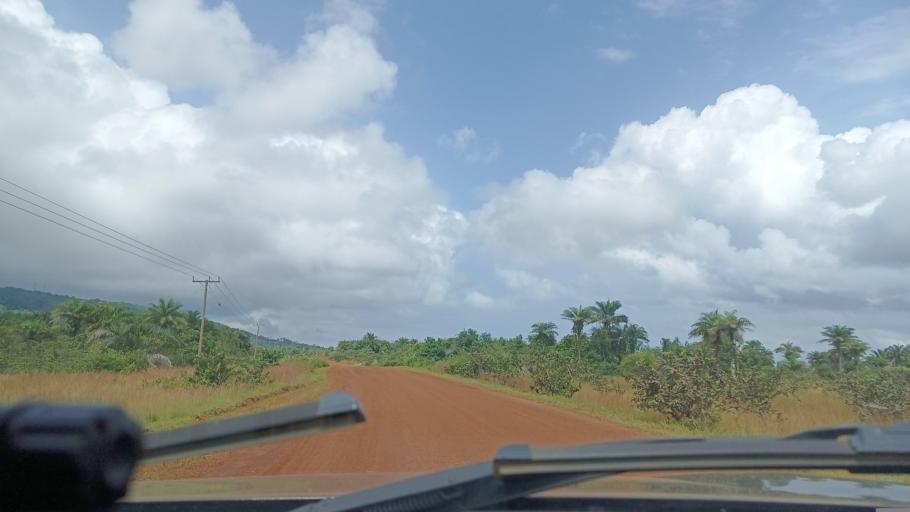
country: LR
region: Grand Cape Mount
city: Robertsport
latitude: 6.7481
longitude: -11.3418
